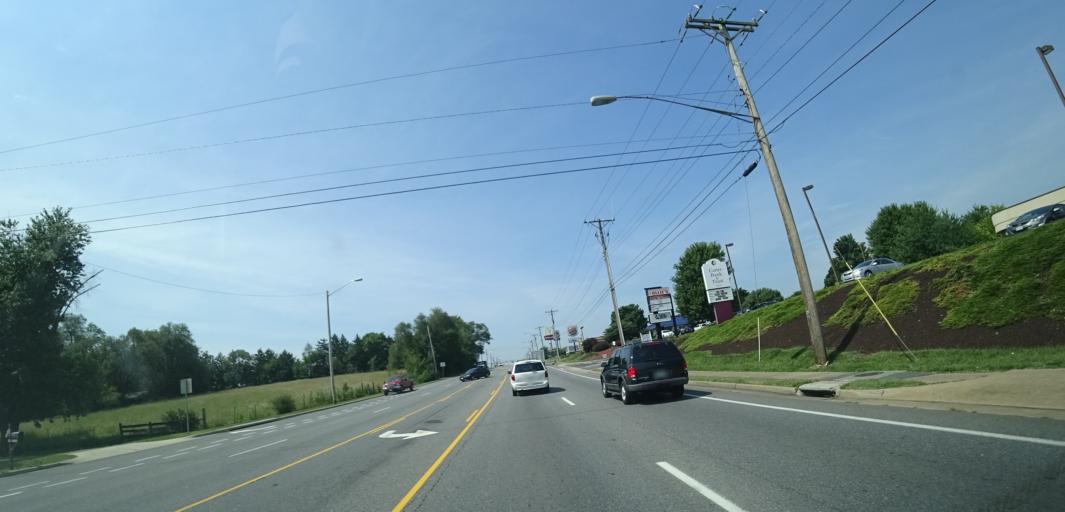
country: US
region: Virginia
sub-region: City of Harrisonburg
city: Harrisonburg
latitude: 38.4218
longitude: -78.8923
